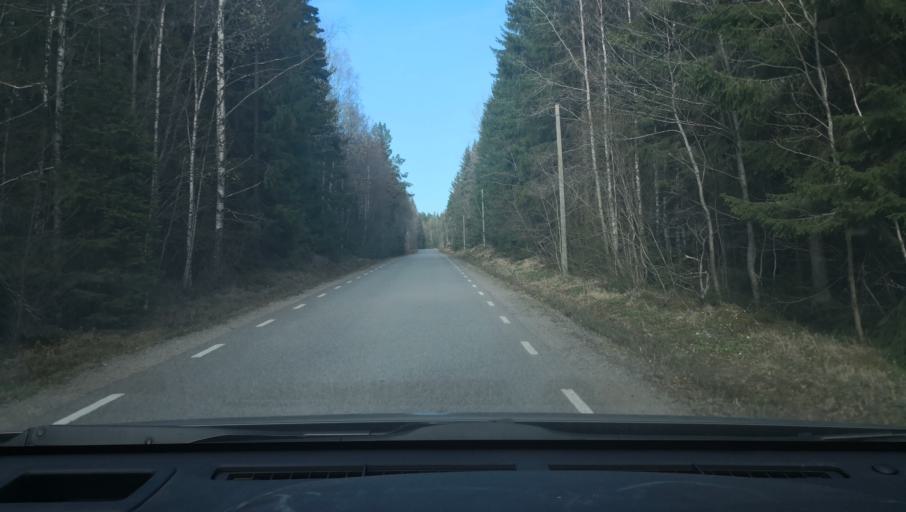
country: SE
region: Uppsala
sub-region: Heby Kommun
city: Heby
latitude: 59.9055
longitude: 16.8168
